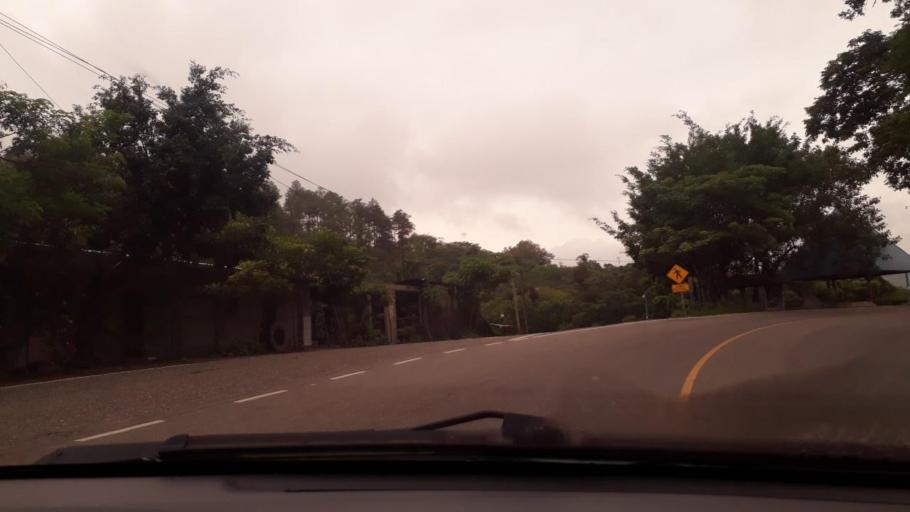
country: GT
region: Chiquimula
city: Concepcion Las Minas
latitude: 14.5588
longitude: -89.4520
